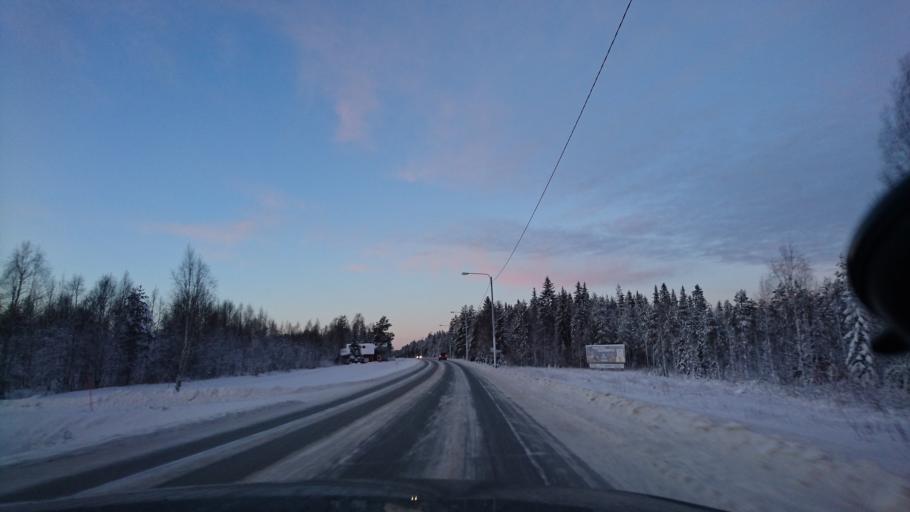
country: FI
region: Lapland
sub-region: Rovaniemi
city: Ranua
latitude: 65.9381
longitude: 26.4875
